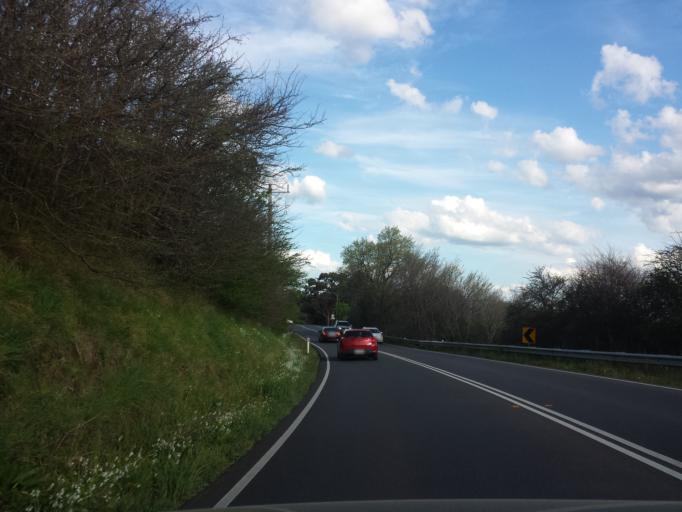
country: AU
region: Victoria
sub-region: Casey
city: Berwick
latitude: -38.0148
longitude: 145.3444
